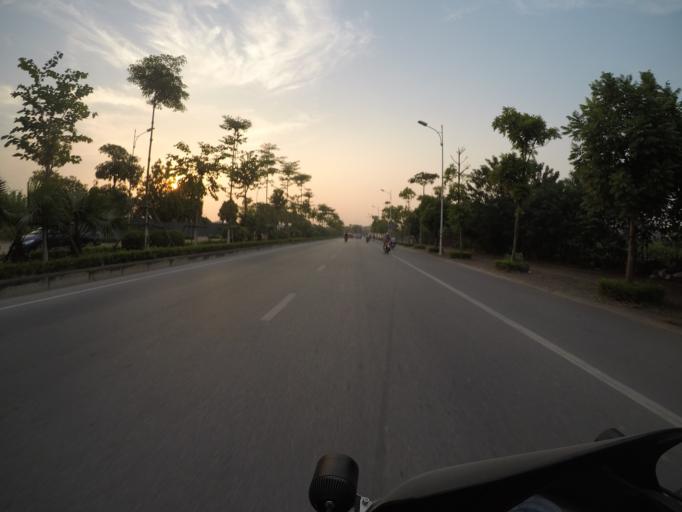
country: VN
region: Ha Noi
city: Hoan Kiem
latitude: 21.0286
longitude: 105.8914
